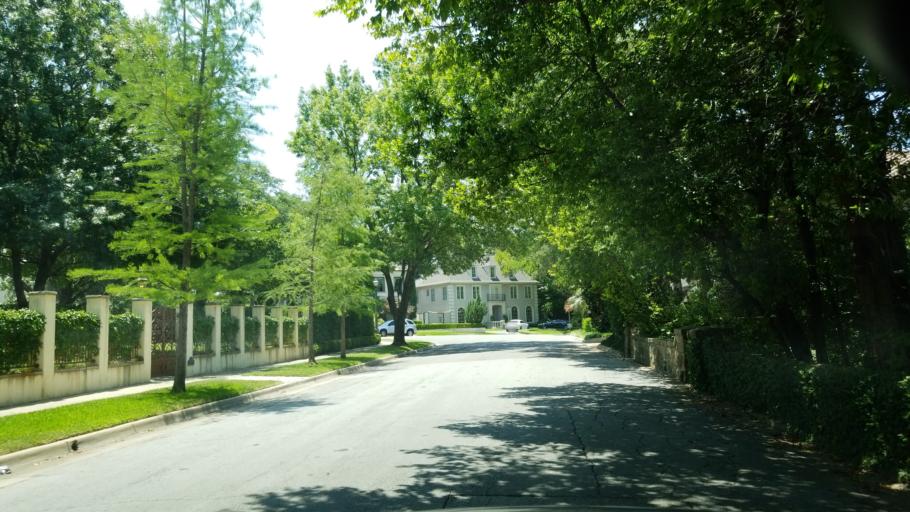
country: US
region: Texas
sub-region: Dallas County
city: Highland Park
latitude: 32.8295
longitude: -96.7944
